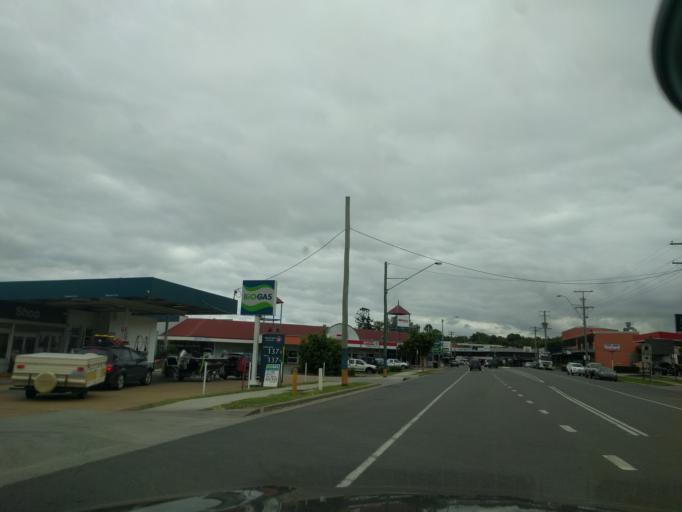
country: AU
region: Queensland
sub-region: Logan
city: Cedar Vale
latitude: -27.9893
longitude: 152.9945
